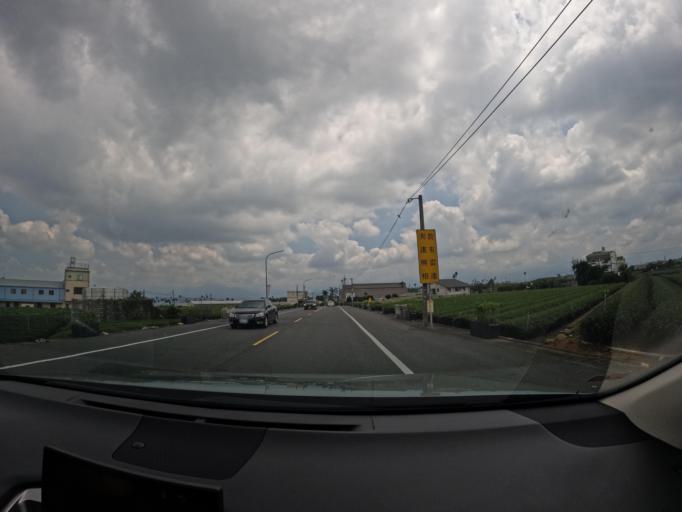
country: TW
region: Taiwan
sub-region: Nantou
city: Nantou
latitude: 23.8327
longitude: 120.6416
